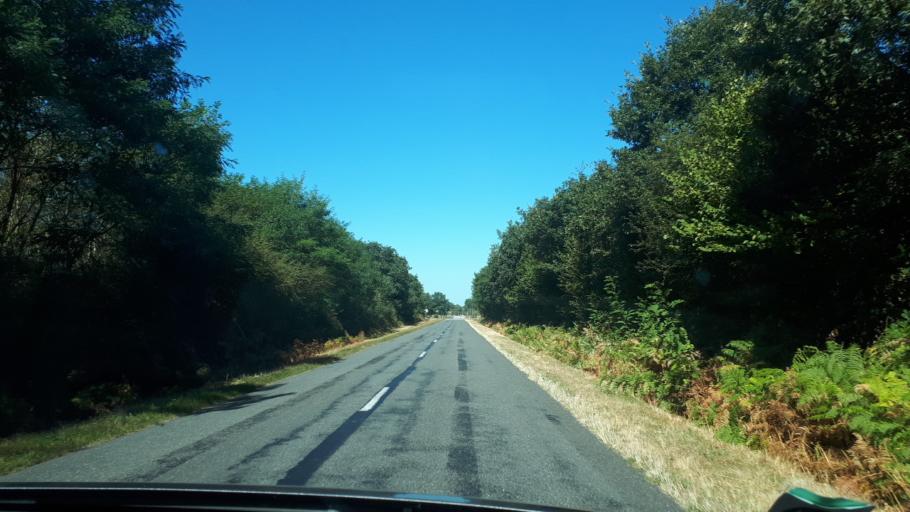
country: FR
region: Centre
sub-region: Departement du Loiret
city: Coullons
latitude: 47.6358
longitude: 2.4516
